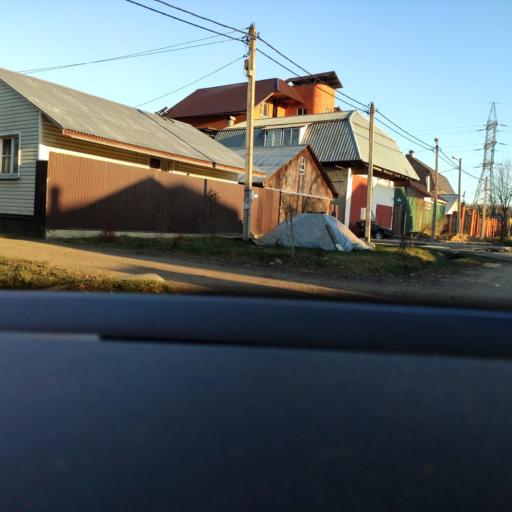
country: RU
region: Moscow
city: Vostochnyy
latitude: 55.8290
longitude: 37.8422
